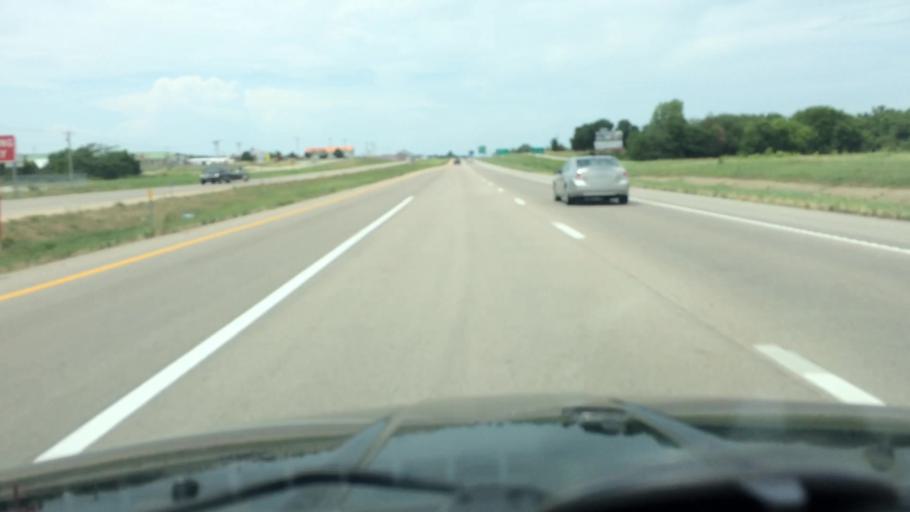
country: US
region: Missouri
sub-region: Polk County
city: Bolivar
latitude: 37.5541
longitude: -93.3877
